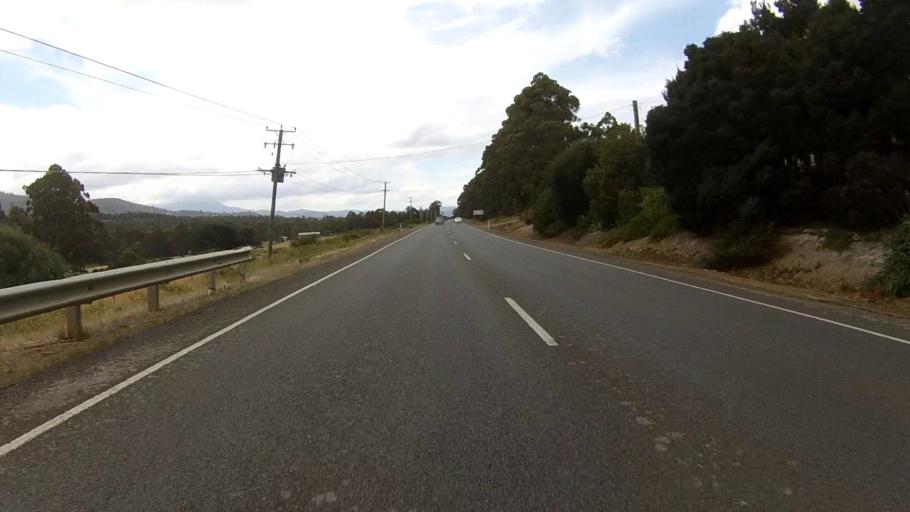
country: AU
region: Tasmania
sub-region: Kingborough
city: Kettering
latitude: -43.0856
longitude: 147.2521
